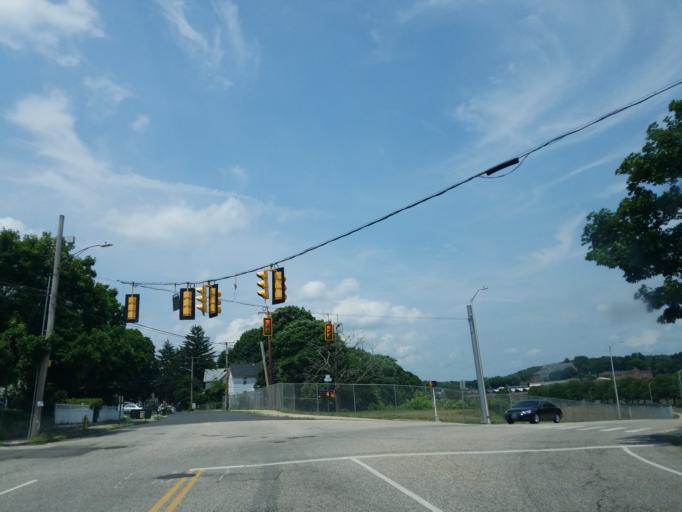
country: US
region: Connecticut
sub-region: New Haven County
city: Ansonia
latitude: 41.3413
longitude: -73.0825
